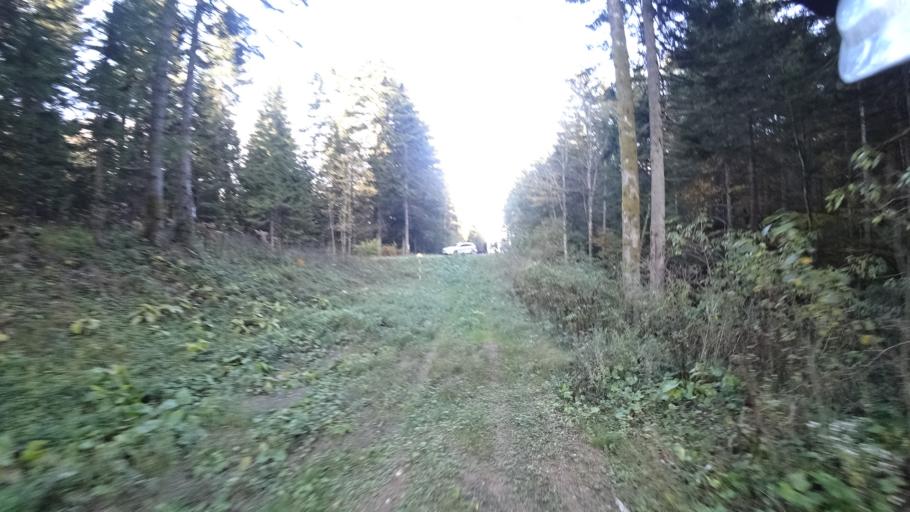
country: HR
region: Karlovacka
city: Plaski
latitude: 44.9820
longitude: 15.4065
